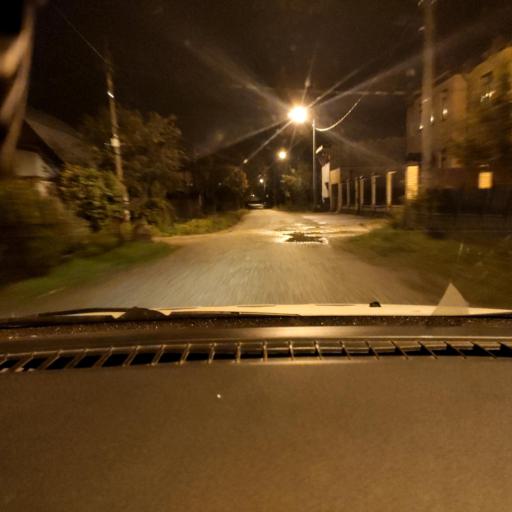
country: RU
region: Perm
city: Kondratovo
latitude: 58.0285
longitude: 55.9956
